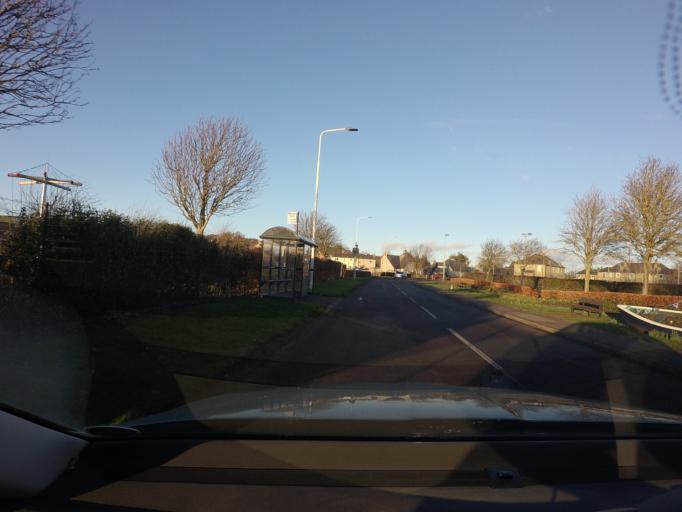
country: GB
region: Scotland
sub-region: Fife
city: Tayport
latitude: 56.4424
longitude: -2.8842
